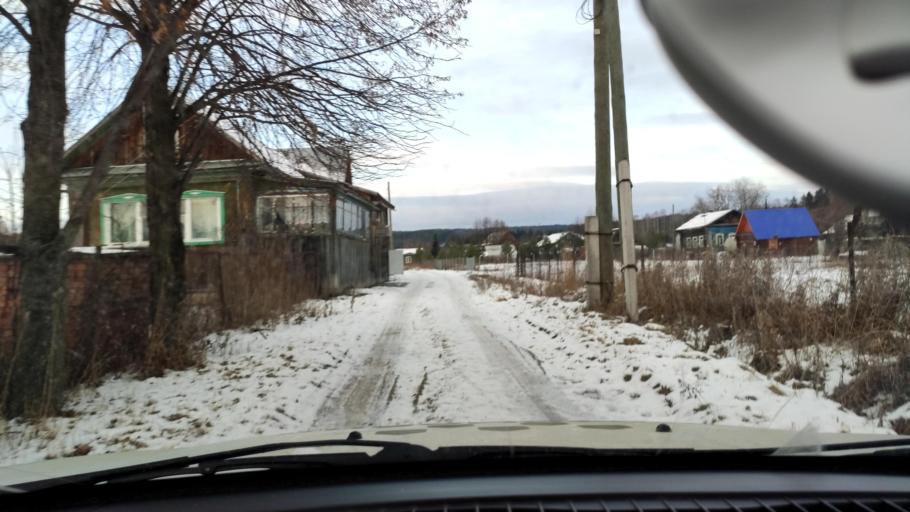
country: RU
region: Perm
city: Lobanovo
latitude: 57.8425
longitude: 56.3711
